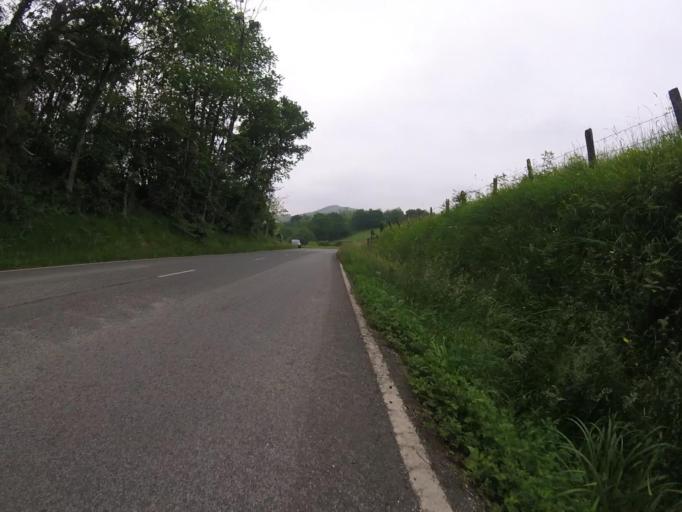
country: ES
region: Navarre
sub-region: Provincia de Navarra
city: Zugarramurdi
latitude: 43.2749
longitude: -1.4977
